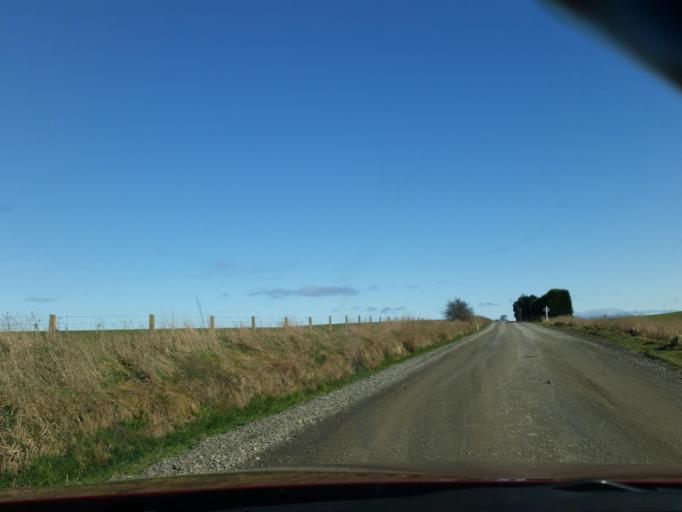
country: NZ
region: Southland
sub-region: Southland District
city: Winton
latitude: -46.2053
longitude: 168.2624
